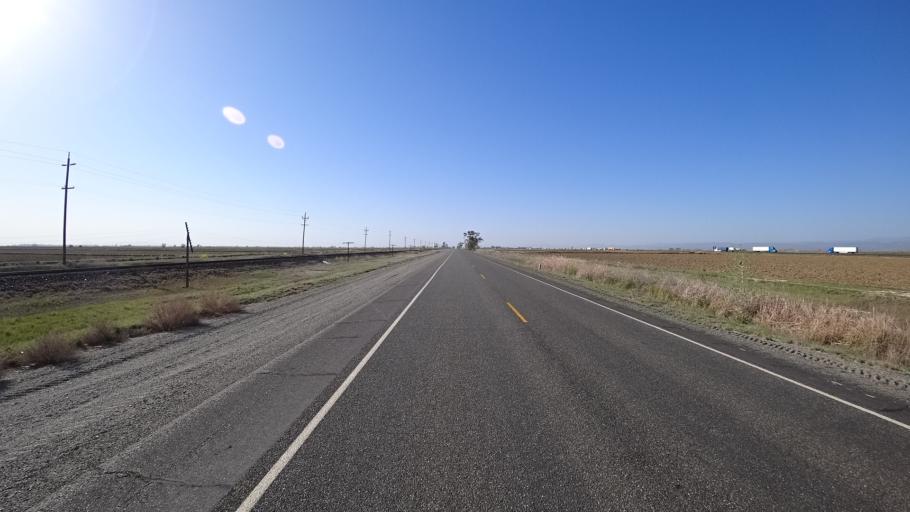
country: US
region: California
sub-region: Glenn County
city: Willows
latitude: 39.4848
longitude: -122.1931
